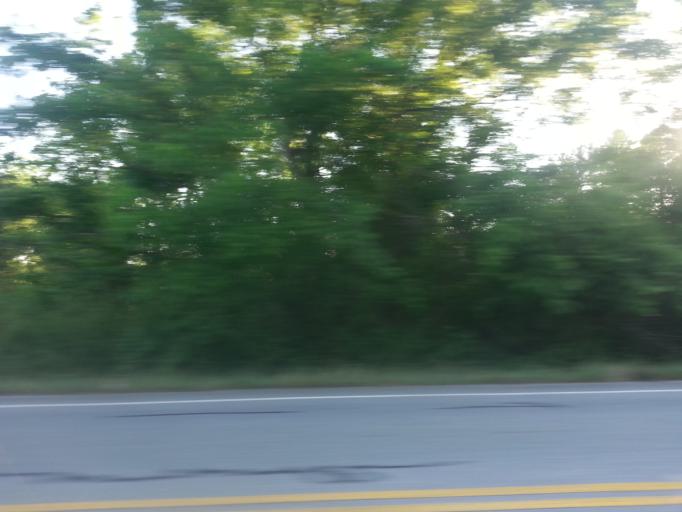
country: US
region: North Carolina
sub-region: Cherokee County
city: Murphy
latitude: 34.9607
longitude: -84.0580
